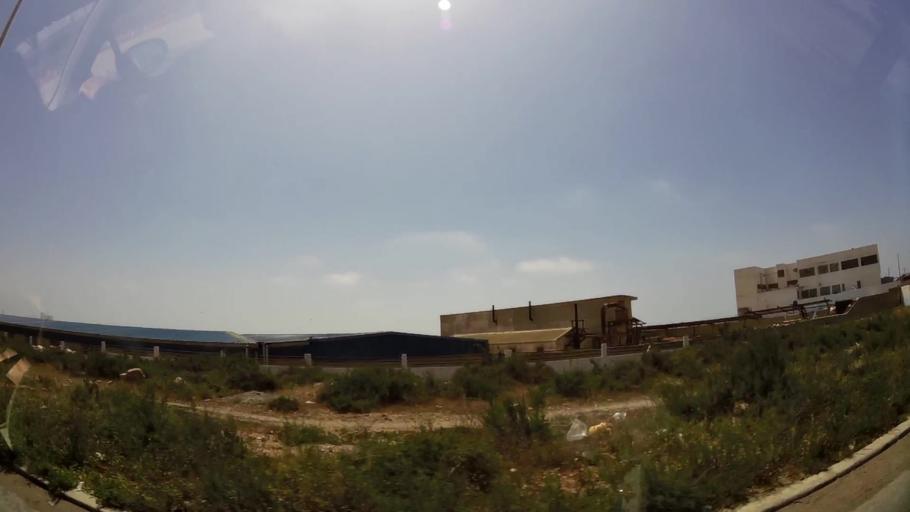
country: MA
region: Souss-Massa-Draa
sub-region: Agadir-Ida-ou-Tnan
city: Aourir
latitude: 30.4427
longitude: -9.6482
